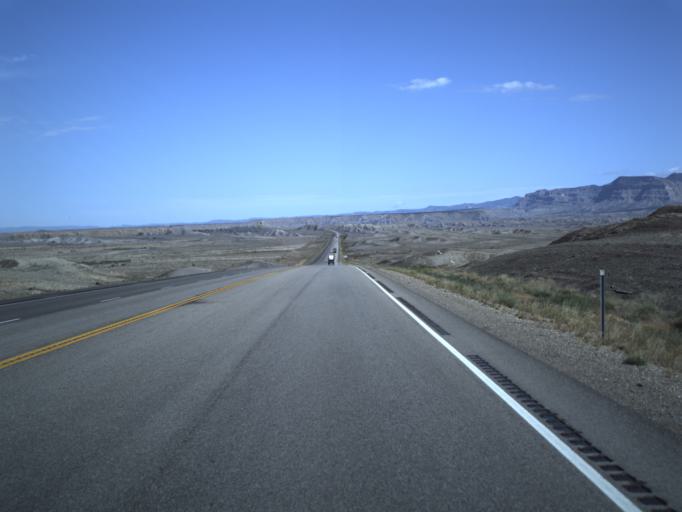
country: US
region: Utah
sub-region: Carbon County
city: East Carbon City
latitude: 39.3040
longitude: -110.3583
